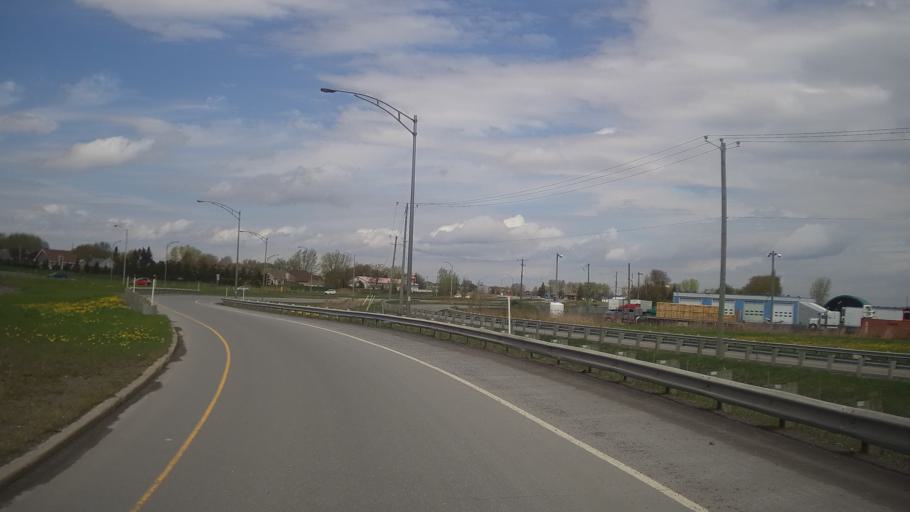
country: CA
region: Quebec
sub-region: Monteregie
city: Saint-Jean-sur-Richelieu
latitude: 45.3144
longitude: -73.2205
